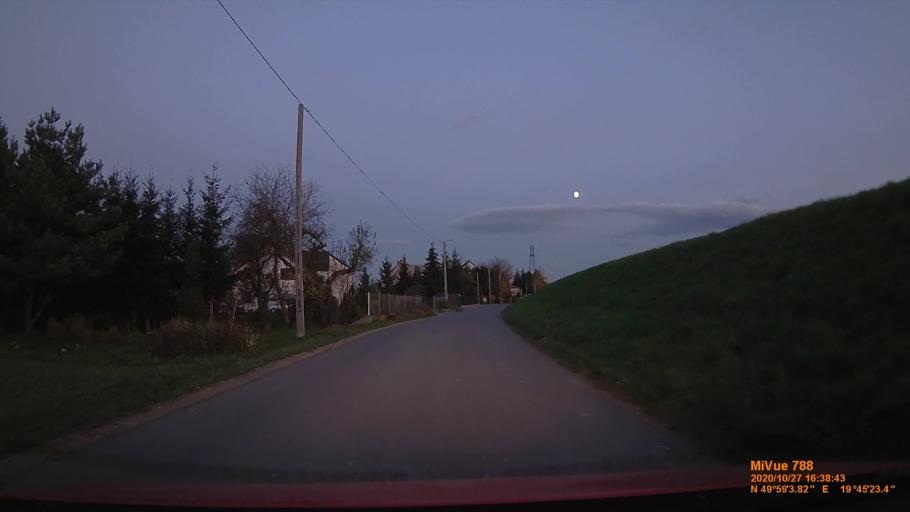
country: PL
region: Lesser Poland Voivodeship
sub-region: Powiat krakowski
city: Raczna
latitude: 49.9844
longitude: 19.7566
